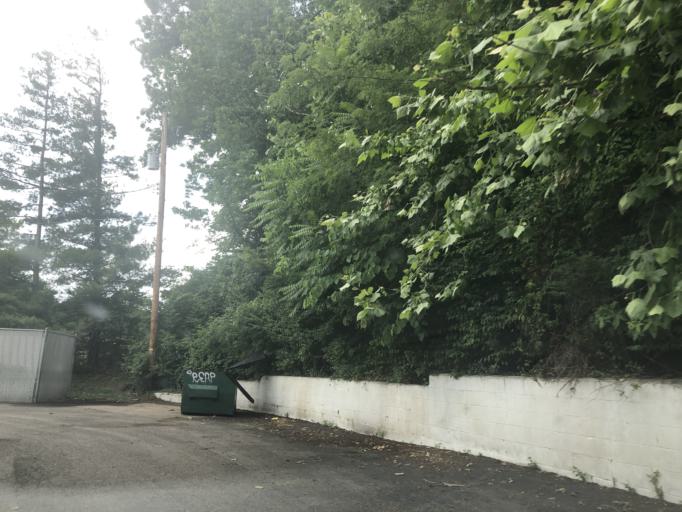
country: US
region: Tennessee
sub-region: Davidson County
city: Belle Meade
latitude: 36.0770
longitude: -86.9195
